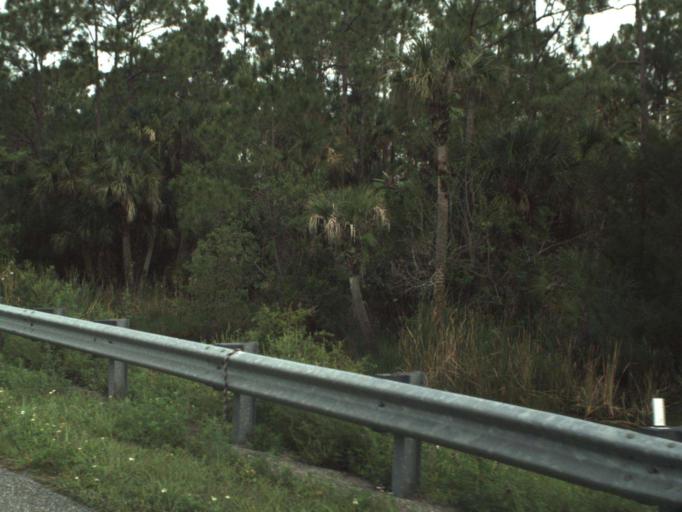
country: US
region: Florida
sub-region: Seminole County
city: Geneva
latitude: 28.7081
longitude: -81.0195
